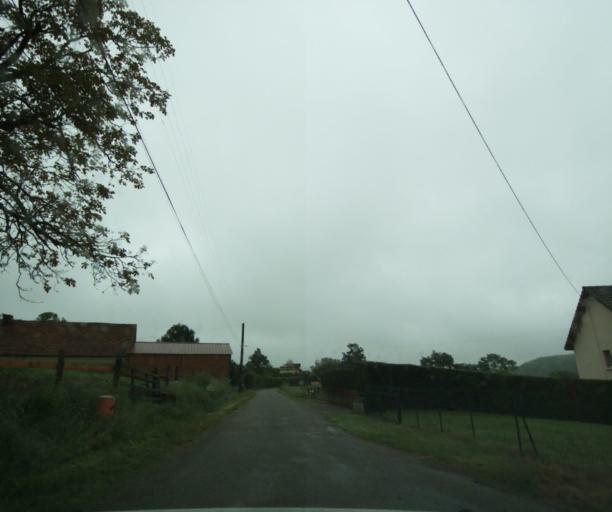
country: FR
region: Bourgogne
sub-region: Departement de Saone-et-Loire
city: Charolles
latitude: 46.4011
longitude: 4.3771
